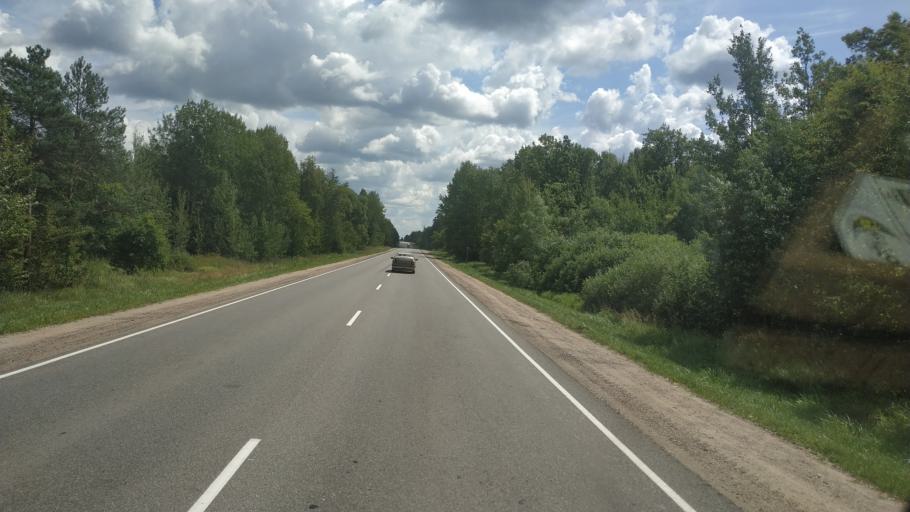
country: BY
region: Mogilev
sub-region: Mahilyowski Rayon
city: Veyno
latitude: 53.8254
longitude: 30.4219
